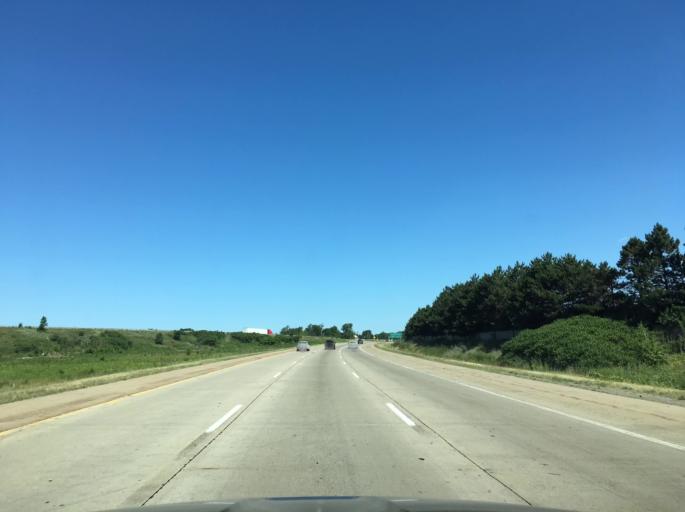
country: US
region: Michigan
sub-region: Oakland County
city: Bloomfield Hills
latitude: 42.6138
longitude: -83.2298
